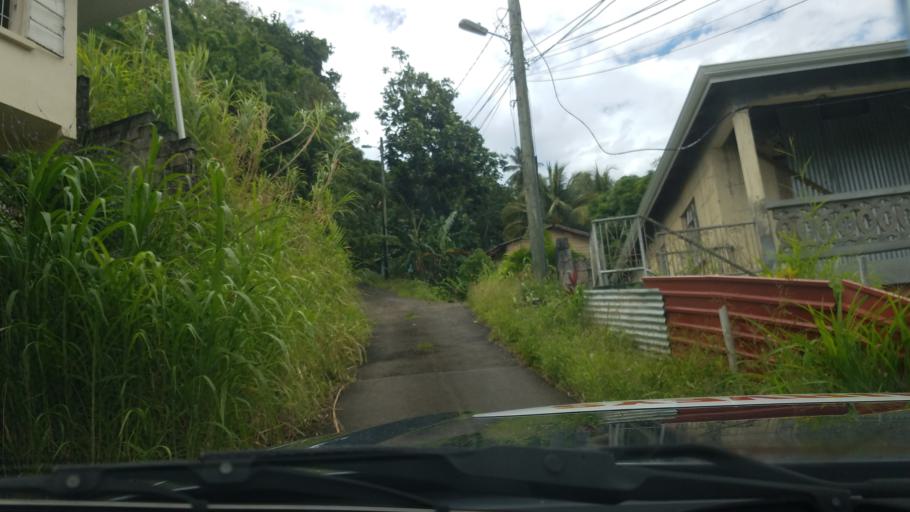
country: LC
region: Castries Quarter
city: Bisee
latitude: 14.0027
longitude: -60.9751
